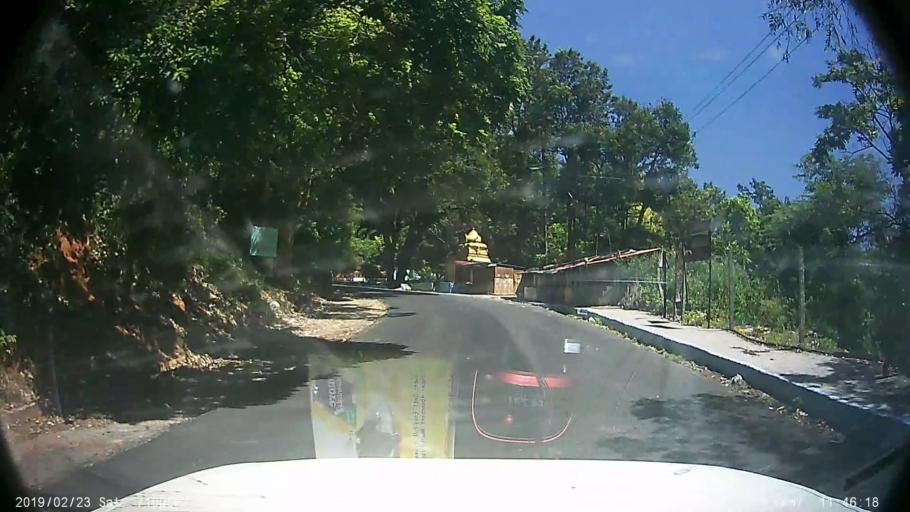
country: IN
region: Tamil Nadu
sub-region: Nilgiri
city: Wellington
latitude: 11.3344
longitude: 76.8260
